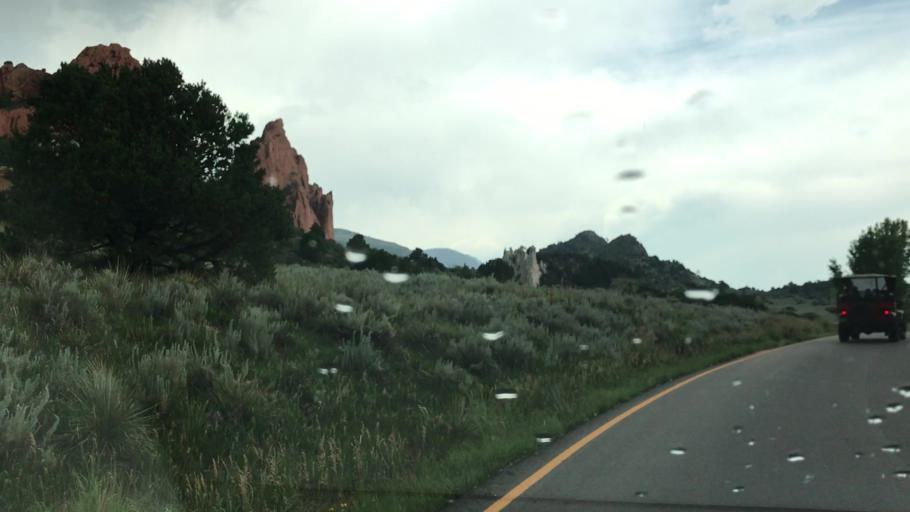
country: US
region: Colorado
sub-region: El Paso County
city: Manitou Springs
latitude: 38.8757
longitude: -104.8783
